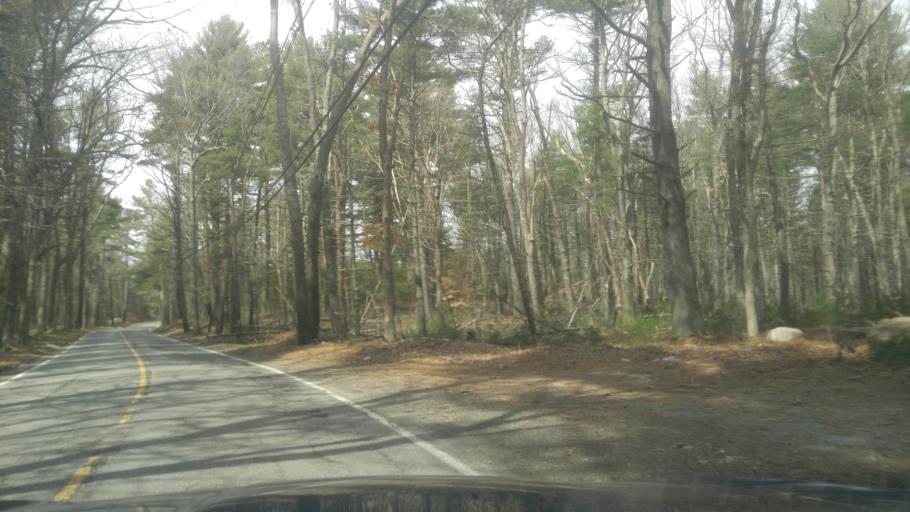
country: US
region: Rhode Island
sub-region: Washington County
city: Exeter
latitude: 41.6420
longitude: -71.5724
